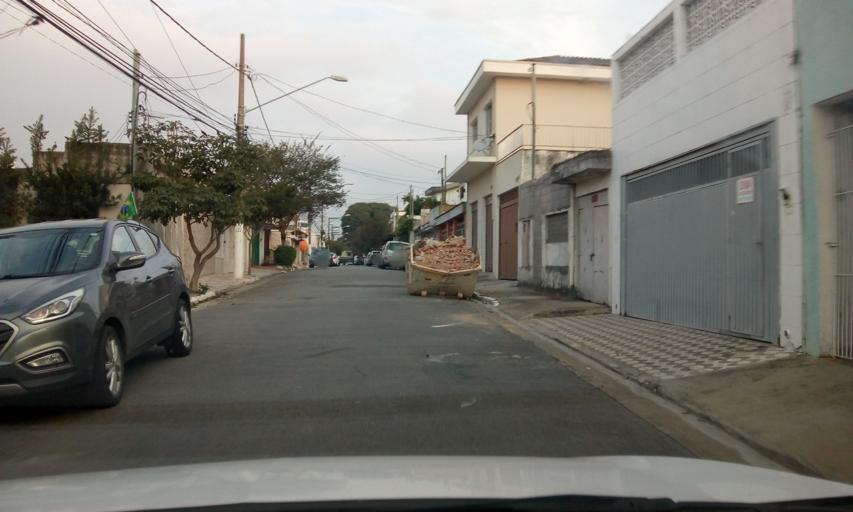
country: BR
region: Sao Paulo
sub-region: Diadema
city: Diadema
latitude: -23.6184
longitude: -46.6446
